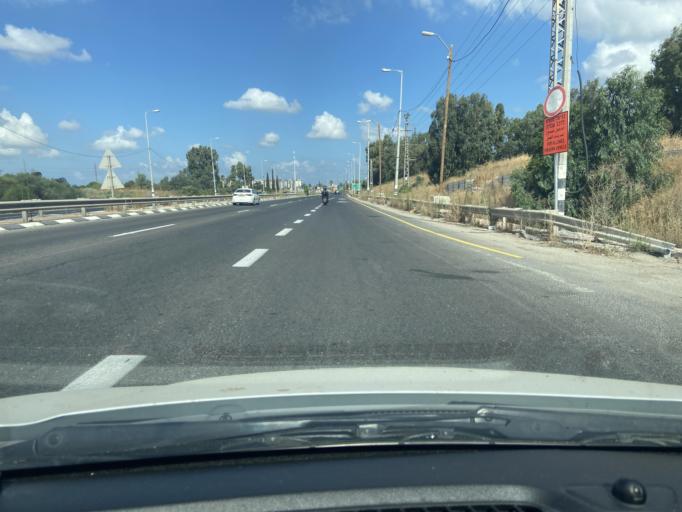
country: IL
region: Central District
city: Yehud
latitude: 32.0257
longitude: 34.8976
